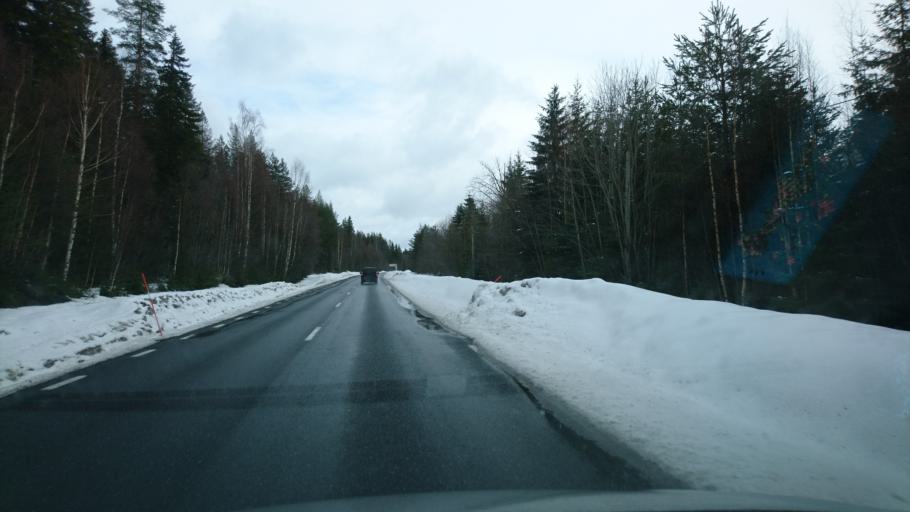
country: SE
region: Vaesternorrland
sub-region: Solleftea Kommun
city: Solleftea
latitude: 63.0469
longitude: 17.0621
